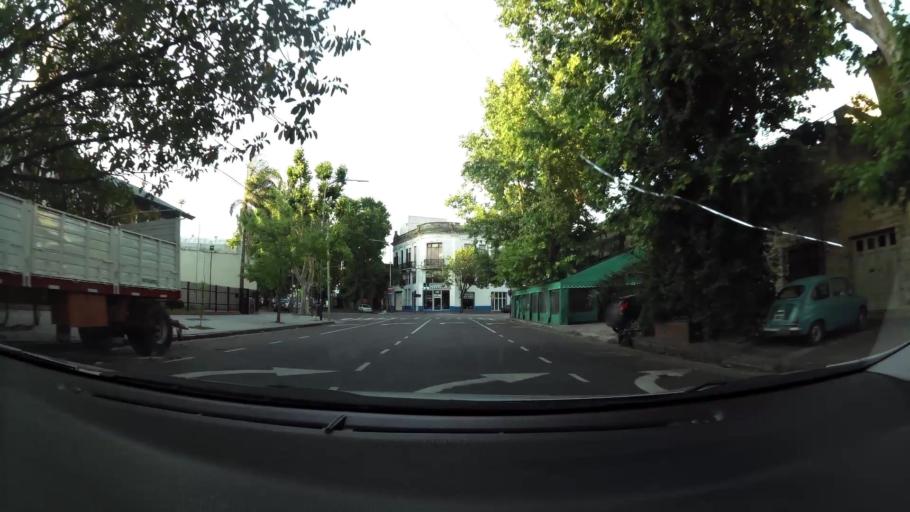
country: AR
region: Buenos Aires F.D.
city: Buenos Aires
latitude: -34.6356
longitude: -58.4105
